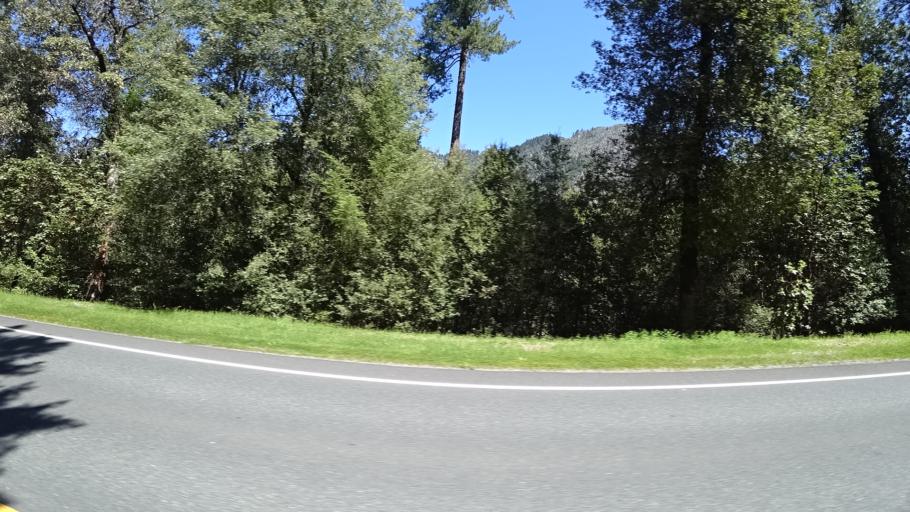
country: US
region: California
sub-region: Humboldt County
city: Willow Creek
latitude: 40.8566
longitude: -123.4938
